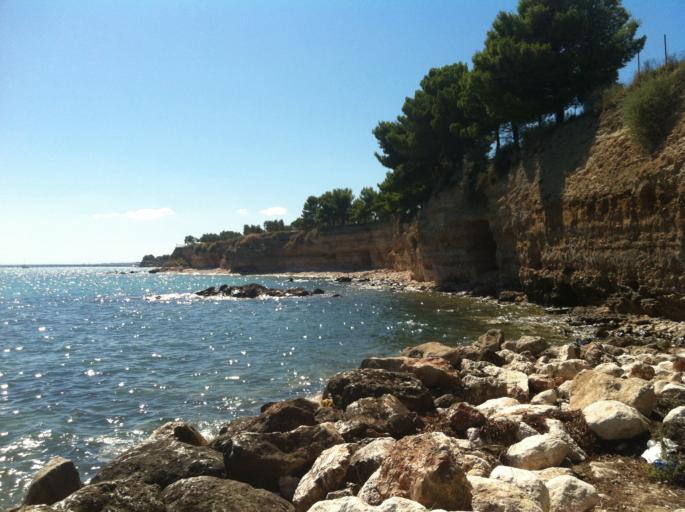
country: IT
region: Apulia
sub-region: Provincia di Foggia
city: Monte Sant'Angelo
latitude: 41.6547
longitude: 15.9769
